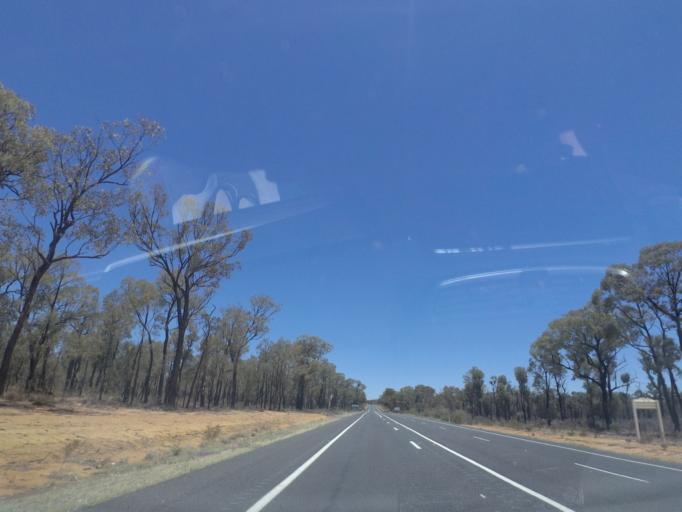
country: AU
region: New South Wales
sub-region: Warrumbungle Shire
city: Coonabarabran
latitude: -30.8789
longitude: 149.4471
